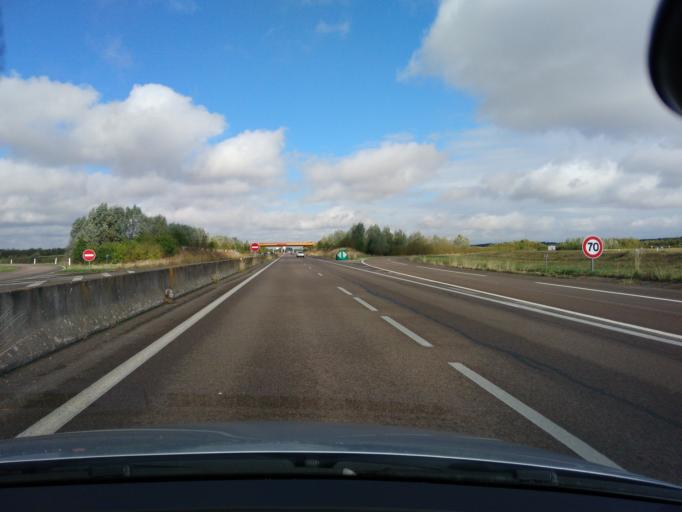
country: FR
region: Haute-Normandie
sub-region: Departement de l'Eure
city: Damville
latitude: 48.8843
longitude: 1.1735
